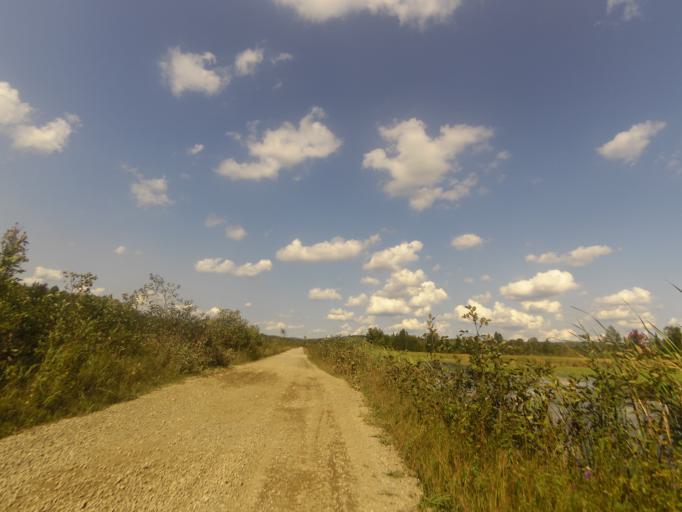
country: CA
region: Ontario
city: Renfrew
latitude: 45.1277
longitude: -76.6881
